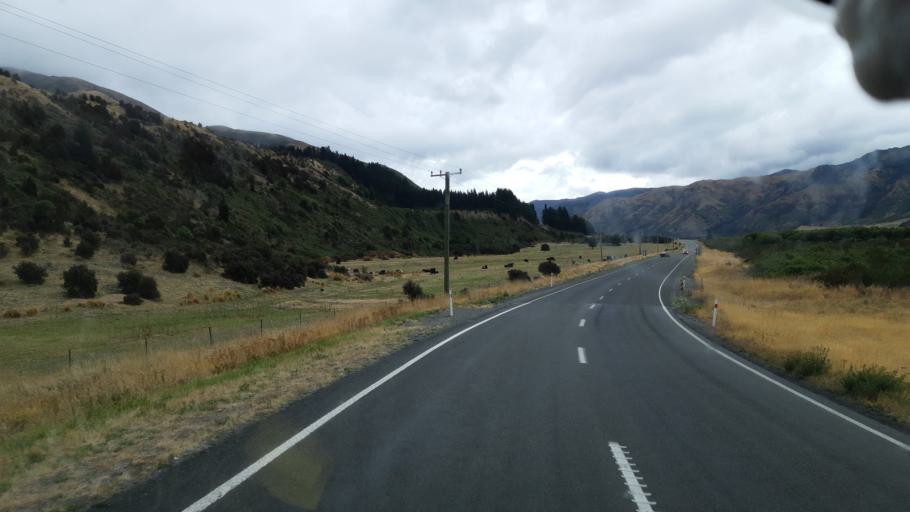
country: NZ
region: Canterbury
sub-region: Hurunui District
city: Amberley
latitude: -42.5712
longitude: 172.7072
